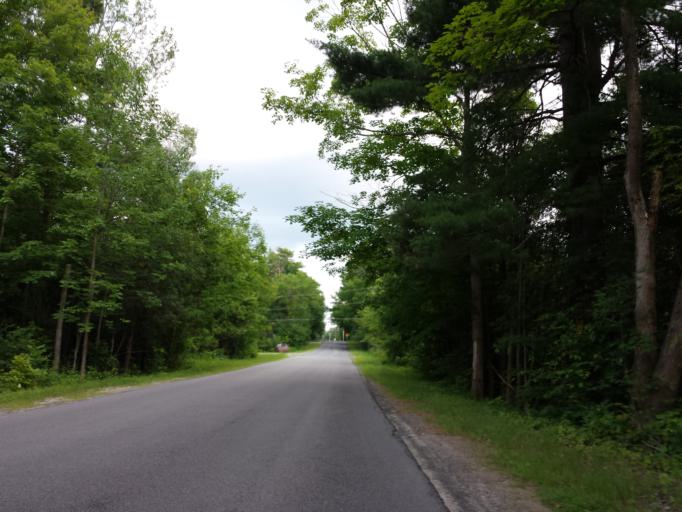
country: US
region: New York
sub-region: St. Lawrence County
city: Norwood
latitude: 44.7231
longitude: -74.9164
